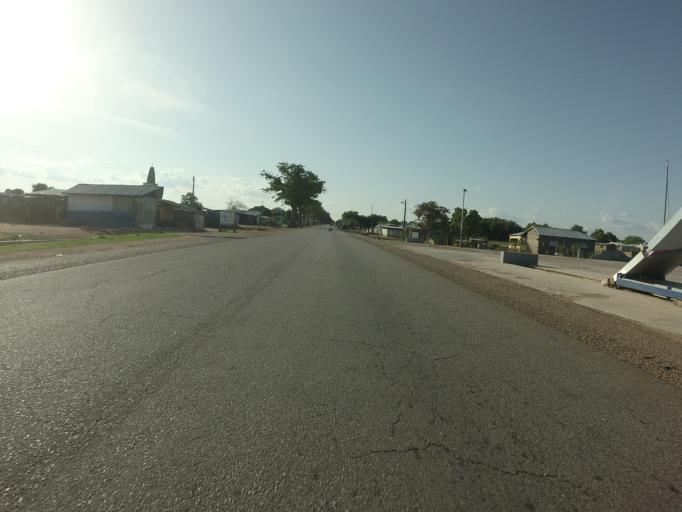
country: GH
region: Upper East
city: Navrongo
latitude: 10.9633
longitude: -1.1000
